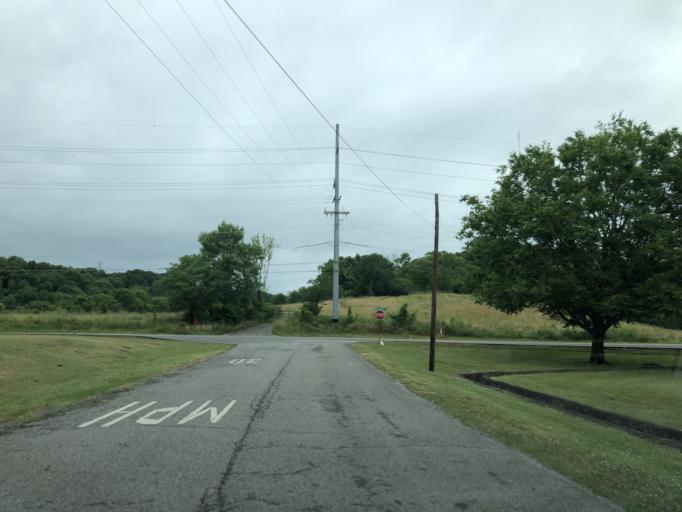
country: US
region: Tennessee
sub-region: Davidson County
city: Goodlettsville
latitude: 36.2667
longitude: -86.7754
